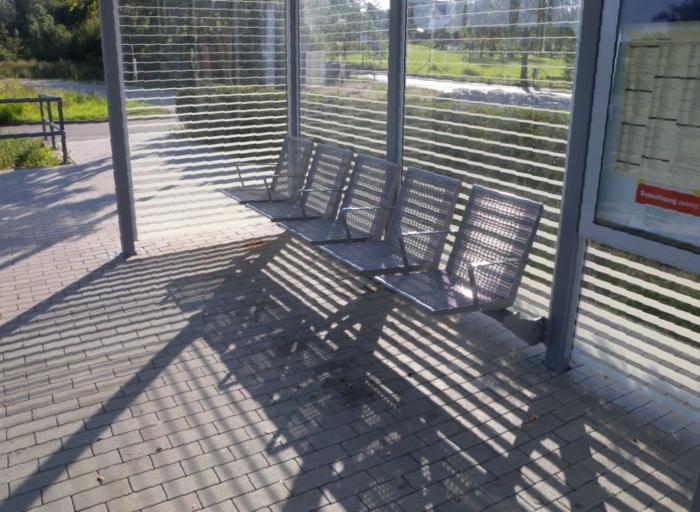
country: DE
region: Bavaria
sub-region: Swabia
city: Ederheim
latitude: 48.8489
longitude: 10.4367
